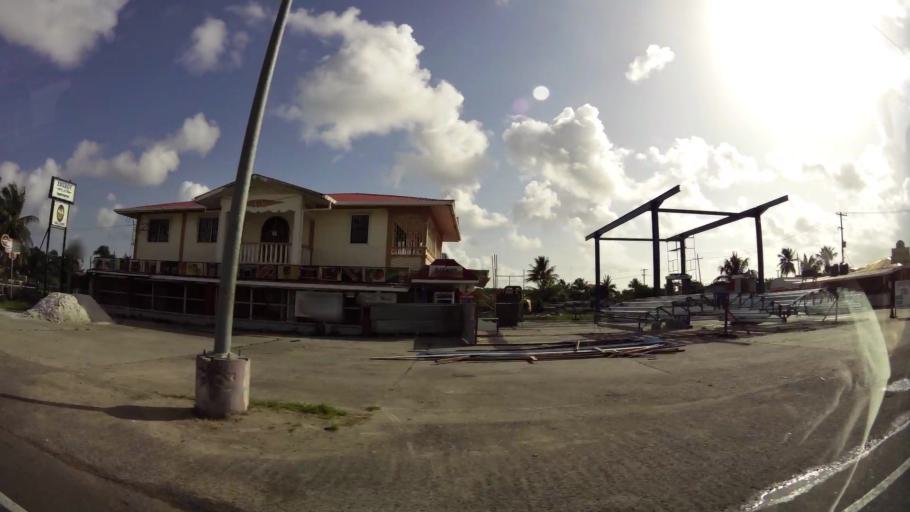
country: GY
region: Demerara-Mahaica
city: Georgetown
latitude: 6.8139
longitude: -58.0677
